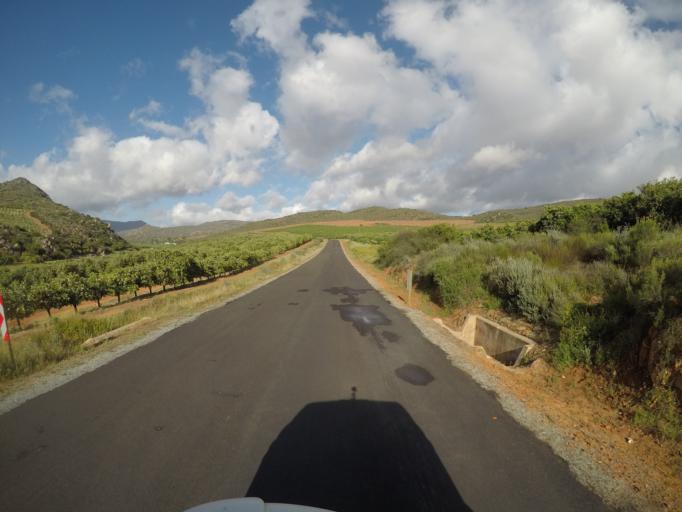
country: ZA
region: Western Cape
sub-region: West Coast District Municipality
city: Clanwilliam
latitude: -32.4307
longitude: 18.9514
